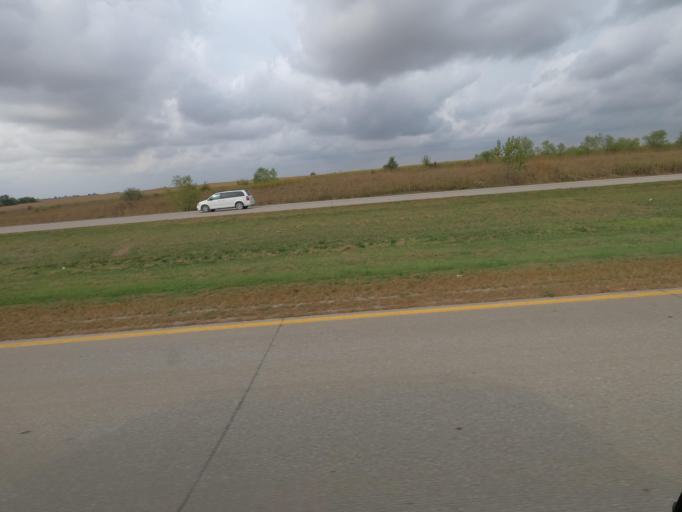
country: US
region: Iowa
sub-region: Wapello County
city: Ottumwa
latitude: 41.0040
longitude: -92.2951
